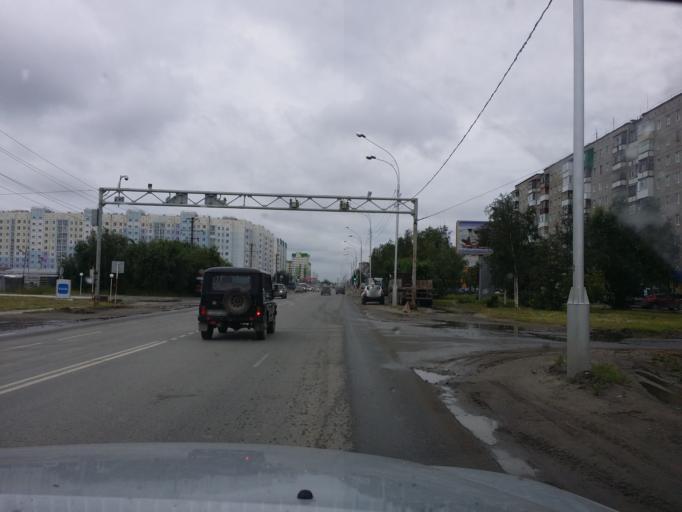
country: RU
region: Khanty-Mansiyskiy Avtonomnyy Okrug
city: Nizhnevartovsk
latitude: 60.9399
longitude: 76.6183
